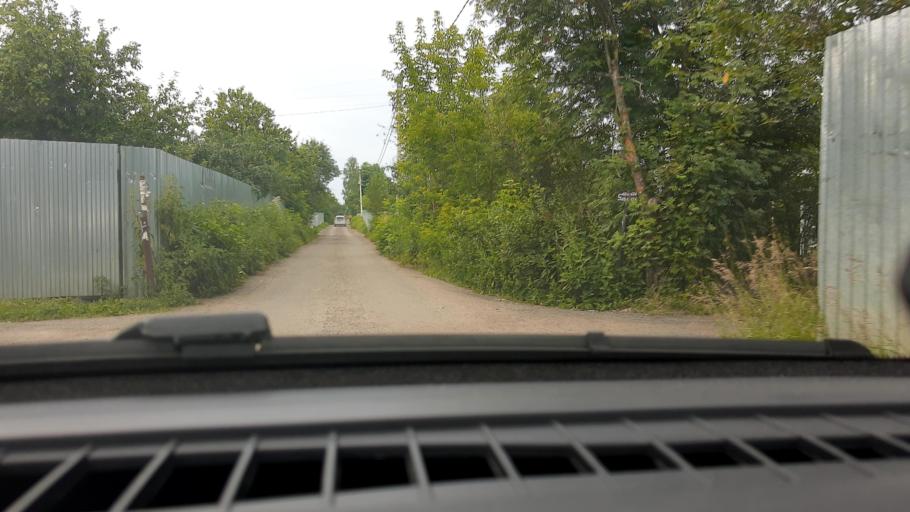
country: RU
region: Nizjnij Novgorod
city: Gorbatovka
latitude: 56.2431
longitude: 43.8177
